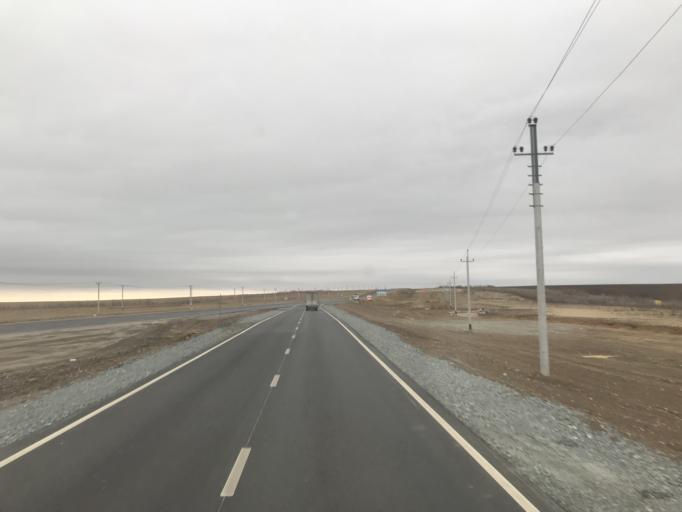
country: KZ
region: Batys Qazaqstan
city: Peremetnoe
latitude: 51.6626
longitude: 51.0070
